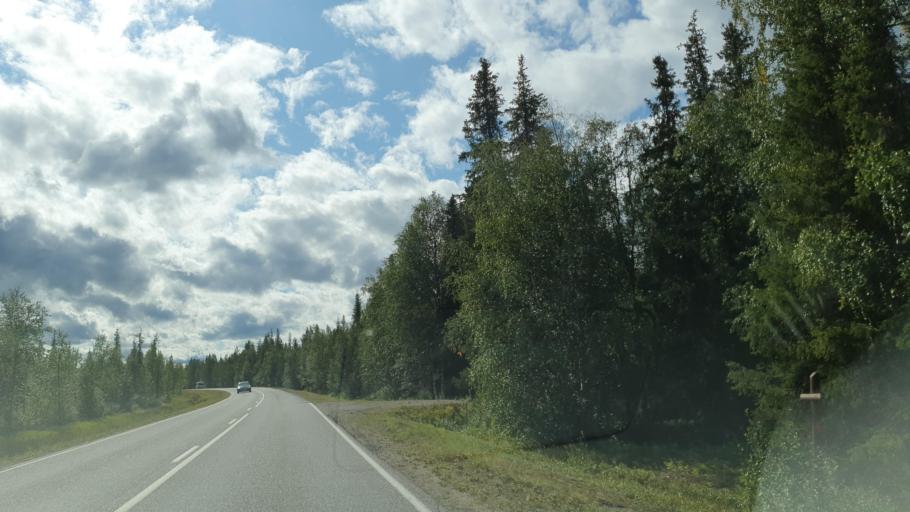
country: FI
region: Lapland
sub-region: Tunturi-Lappi
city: Muonio
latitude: 67.8819
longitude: 24.2100
